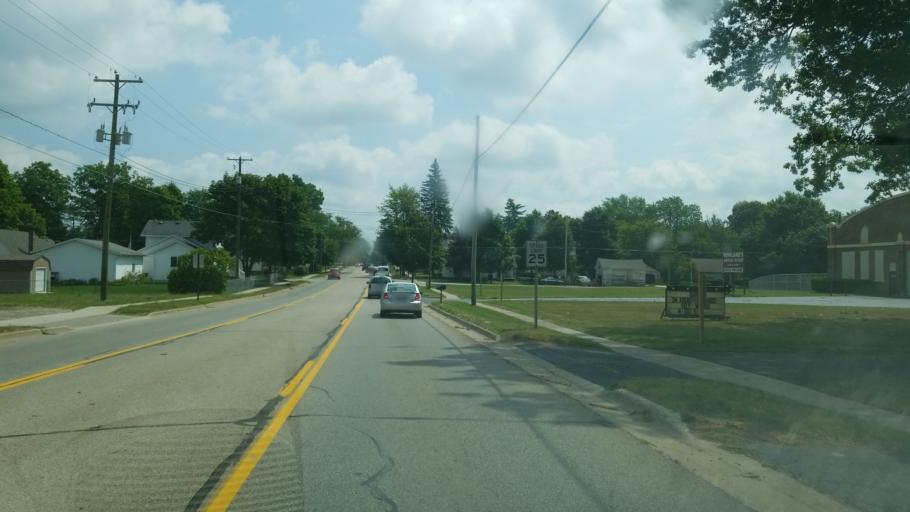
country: US
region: Michigan
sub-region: Kent County
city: Cedar Springs
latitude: 43.2200
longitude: -85.5550
